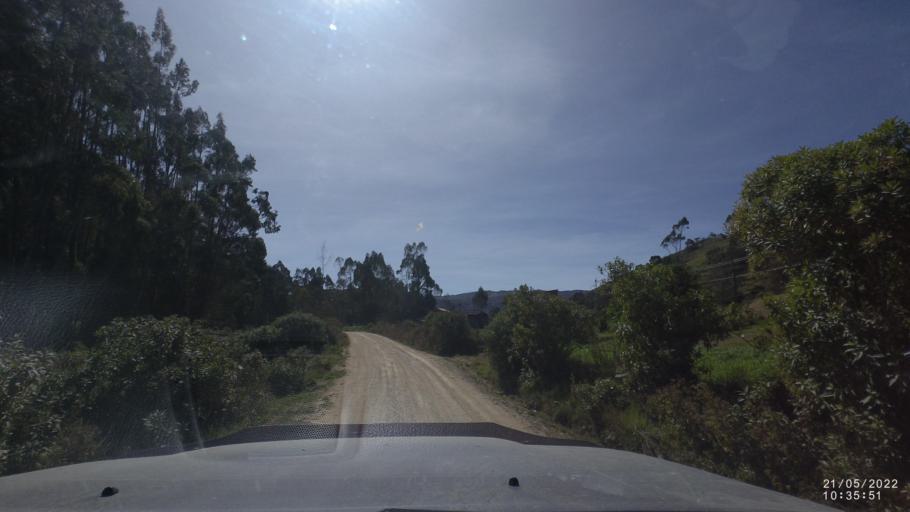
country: BO
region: Cochabamba
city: Colomi
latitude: -17.3166
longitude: -65.9257
